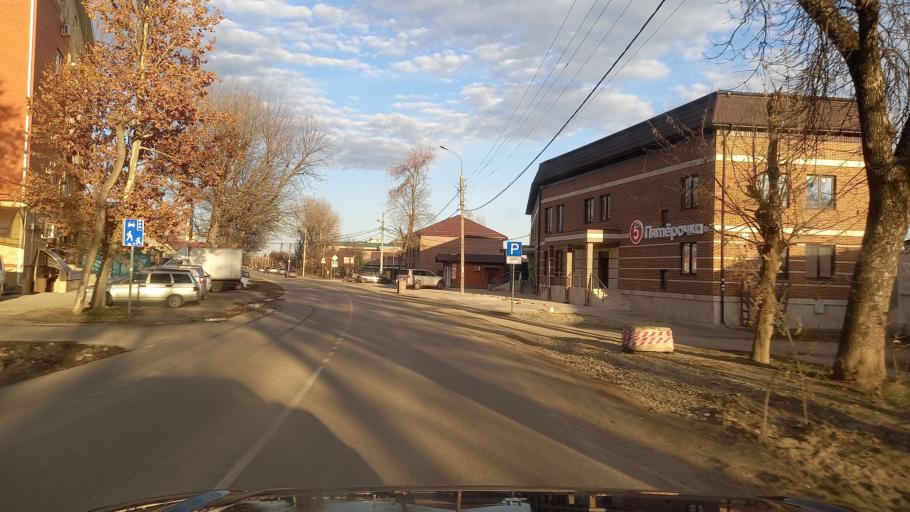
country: RU
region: Krasnodarskiy
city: Pashkovskiy
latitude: 45.0154
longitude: 39.1073
